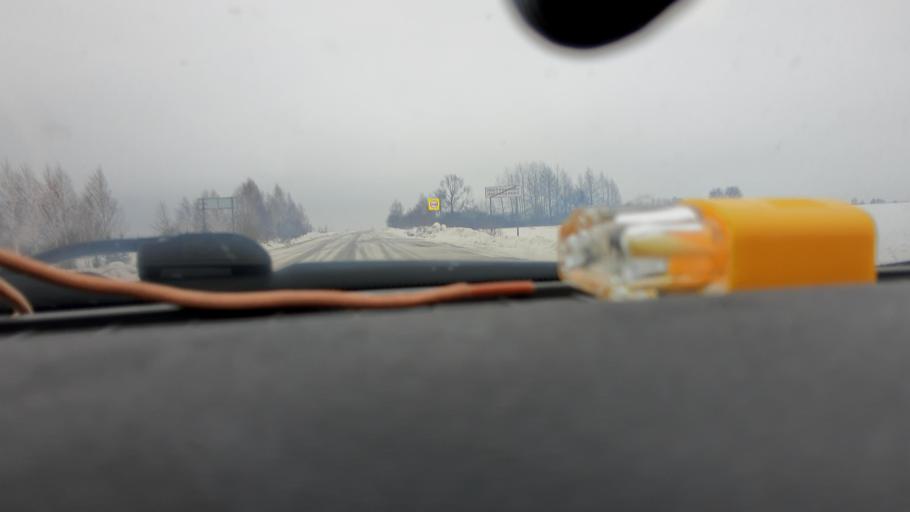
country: RU
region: Bashkortostan
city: Iglino
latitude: 54.6315
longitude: 56.4254
